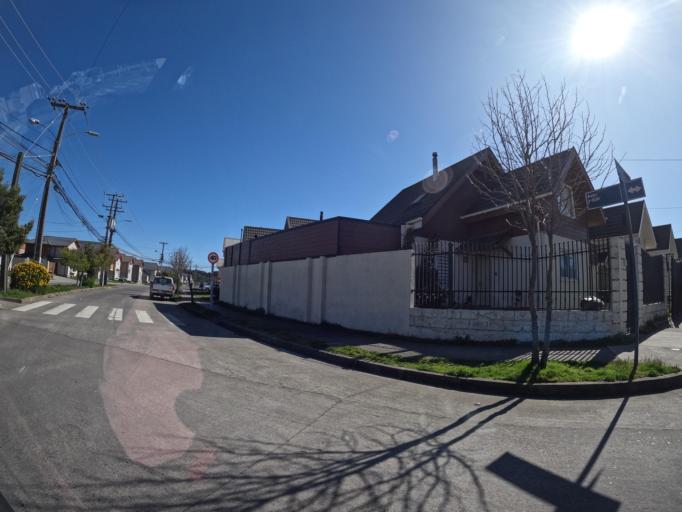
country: CL
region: Biobio
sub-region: Provincia de Concepcion
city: Concepcion
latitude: -36.8900
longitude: -73.1460
